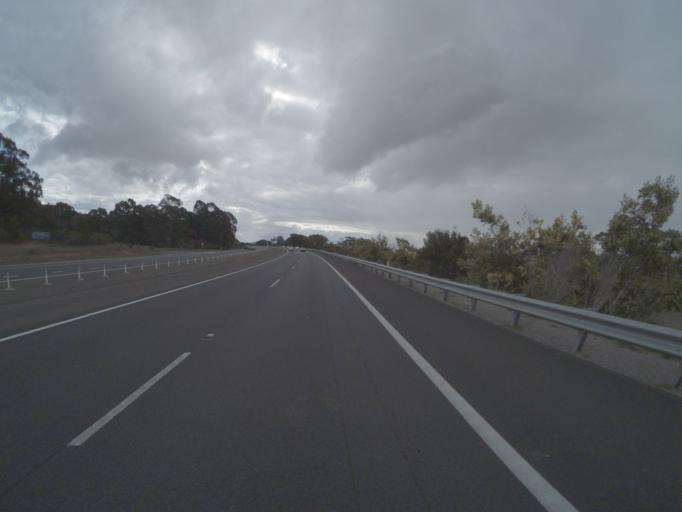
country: AU
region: New South Wales
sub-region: Goulburn Mulwaree
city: Goulburn
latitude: -34.7338
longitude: 149.8299
